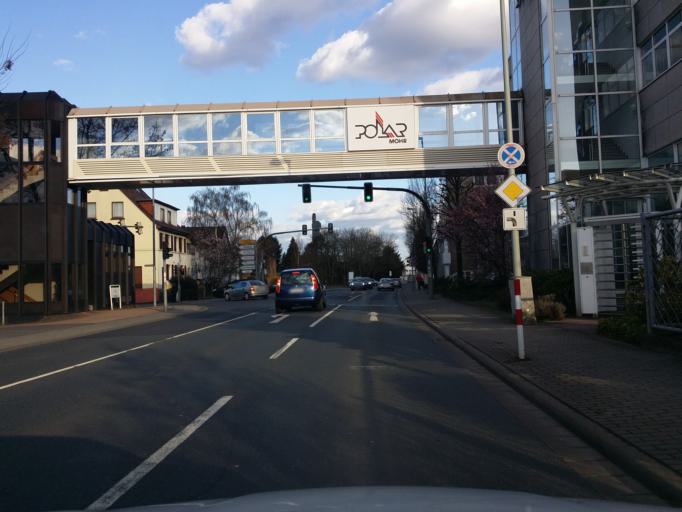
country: DE
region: Hesse
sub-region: Regierungsbezirk Darmstadt
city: Hofheim am Taunus
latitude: 50.0832
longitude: 8.4514
